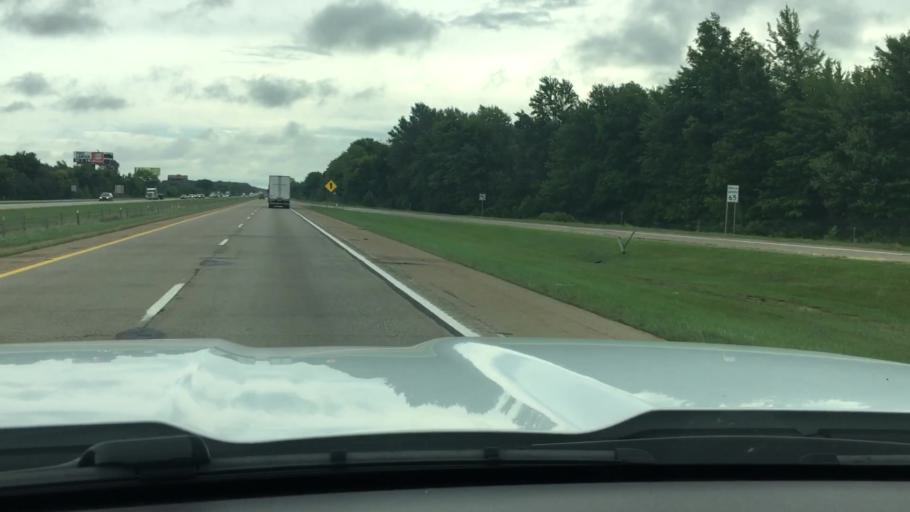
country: US
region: Michigan
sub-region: Ionia County
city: Ionia
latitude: 42.8786
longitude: -85.0339
